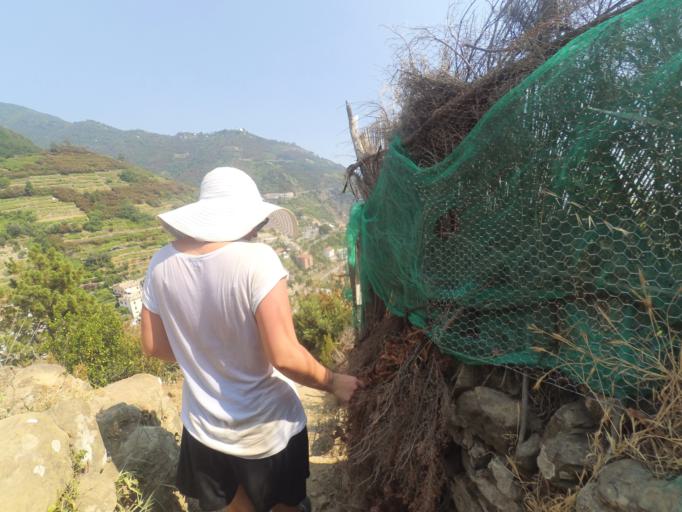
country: IT
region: Liguria
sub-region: Provincia di La Spezia
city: Riomaggiore
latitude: 44.1032
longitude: 9.7344
